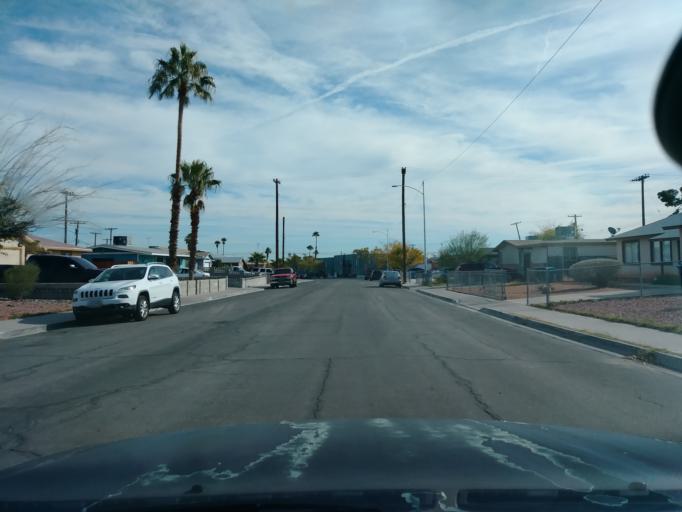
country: US
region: Nevada
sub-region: Clark County
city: Spring Valley
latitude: 36.1611
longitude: -115.2381
